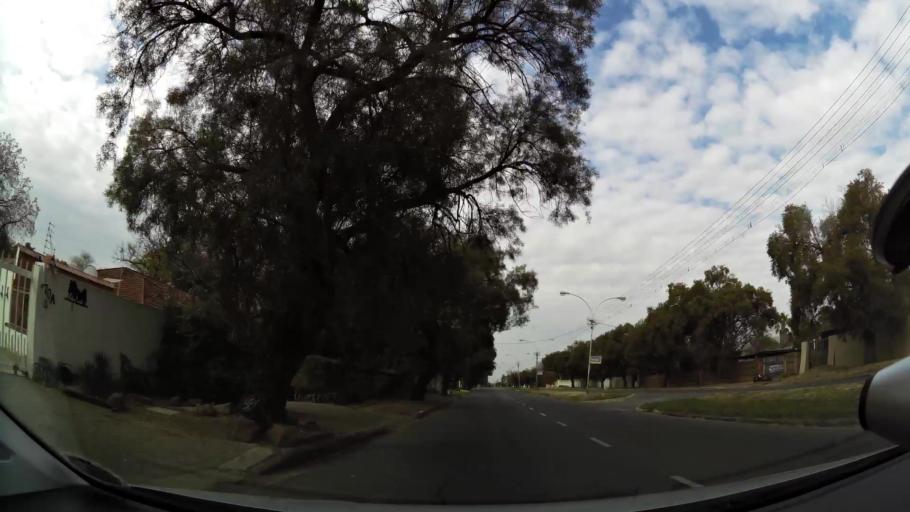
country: ZA
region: Orange Free State
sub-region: Mangaung Metropolitan Municipality
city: Bloemfontein
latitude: -29.0897
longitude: 26.2381
